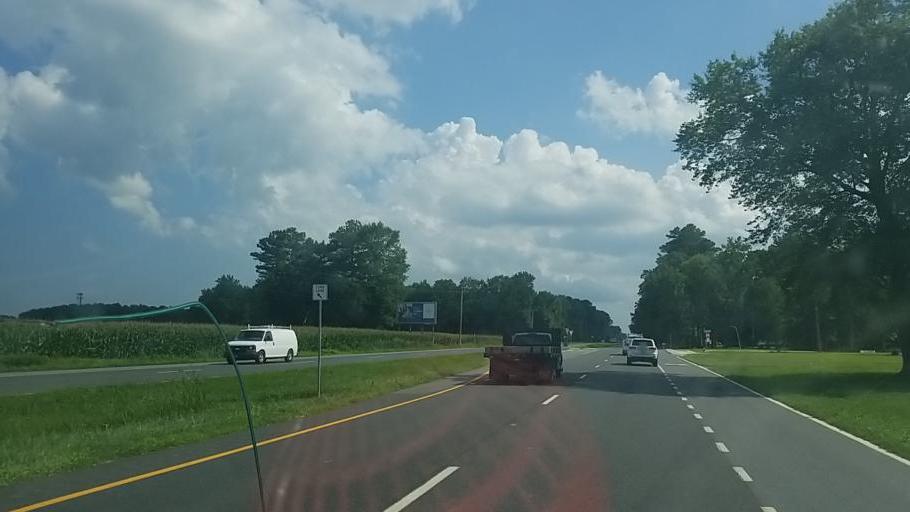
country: US
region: Delaware
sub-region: Sussex County
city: Selbyville
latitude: 38.4757
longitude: -75.2351
